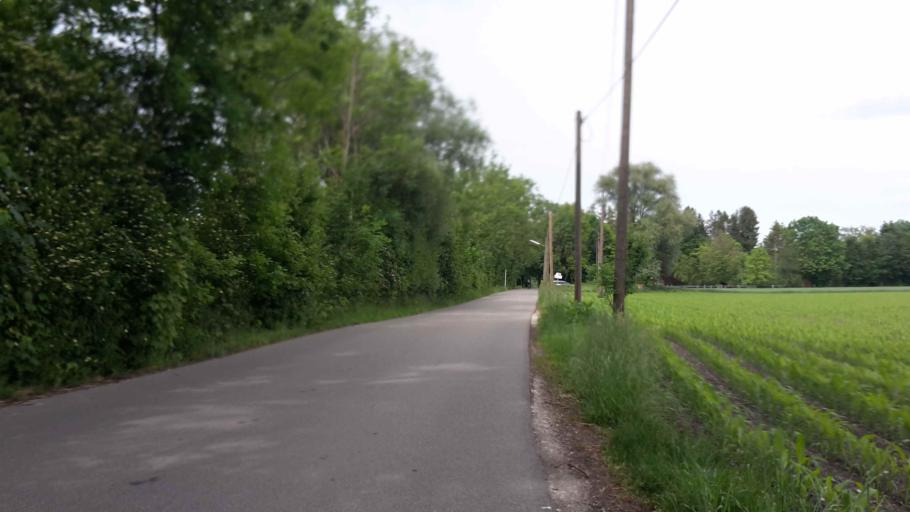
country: DE
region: Bavaria
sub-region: Upper Bavaria
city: Dachau
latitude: 48.2246
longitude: 11.4285
